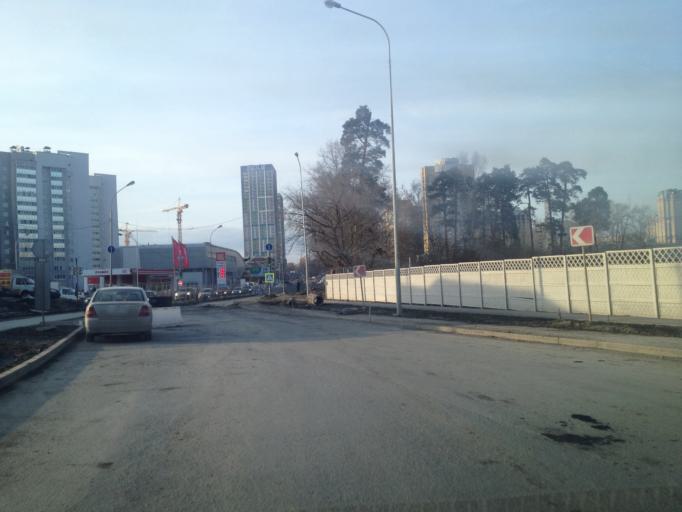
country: RU
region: Sverdlovsk
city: Sovkhoznyy
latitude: 56.7957
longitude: 60.5962
